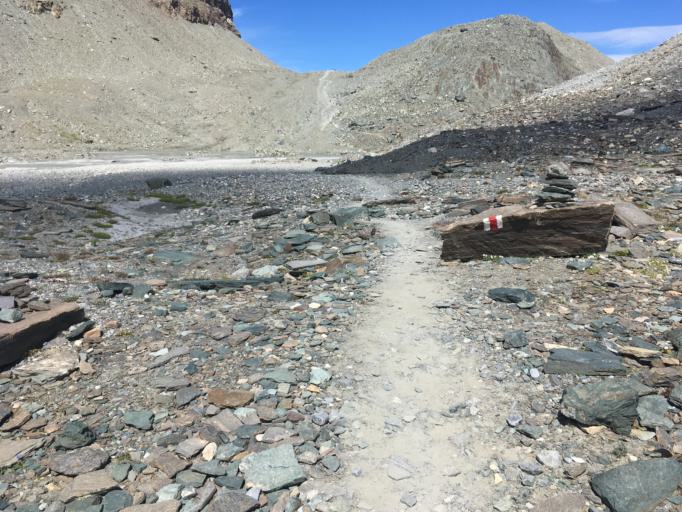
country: CH
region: Valais
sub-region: Visp District
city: Zermatt
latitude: 45.9832
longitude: 7.6911
